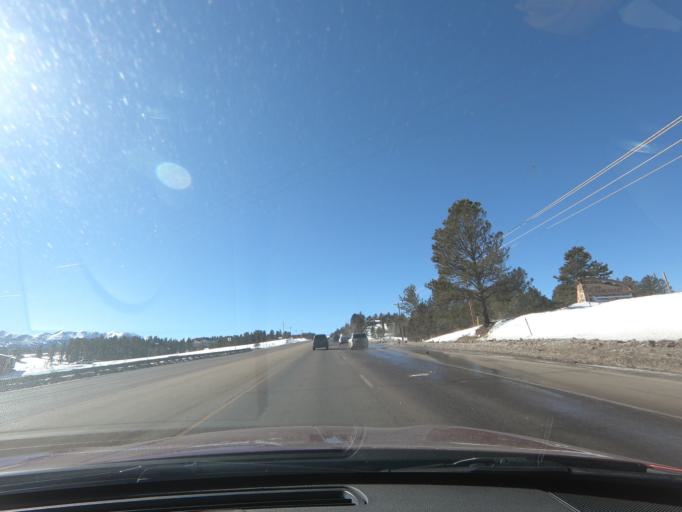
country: US
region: Colorado
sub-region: Teller County
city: Woodland Park
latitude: 38.9794
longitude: -105.0728
